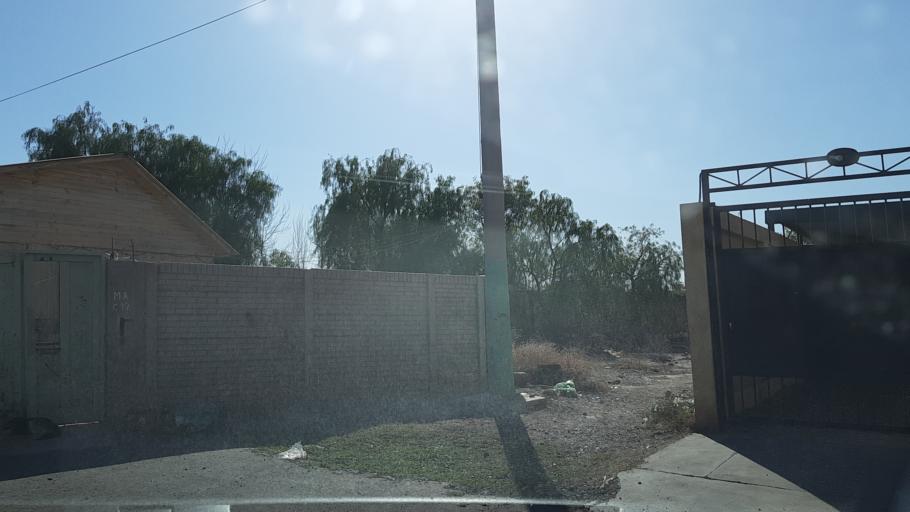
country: AR
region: San Juan
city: San Juan
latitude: -31.5441
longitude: -68.5781
